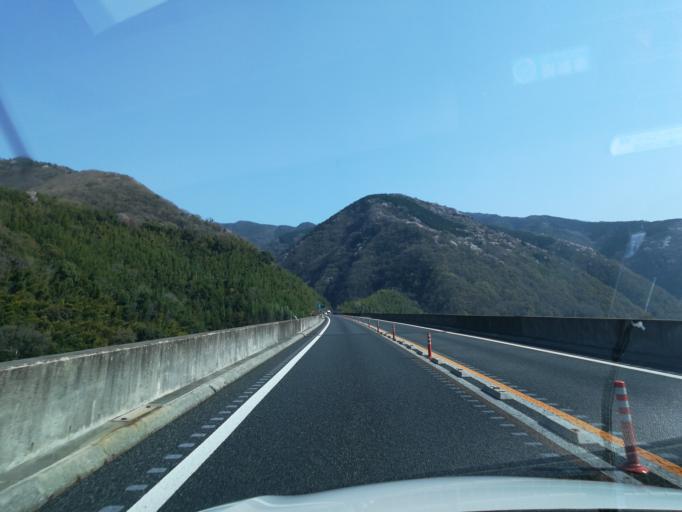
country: JP
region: Tokushima
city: Ikedacho
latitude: 34.0459
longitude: 133.9129
